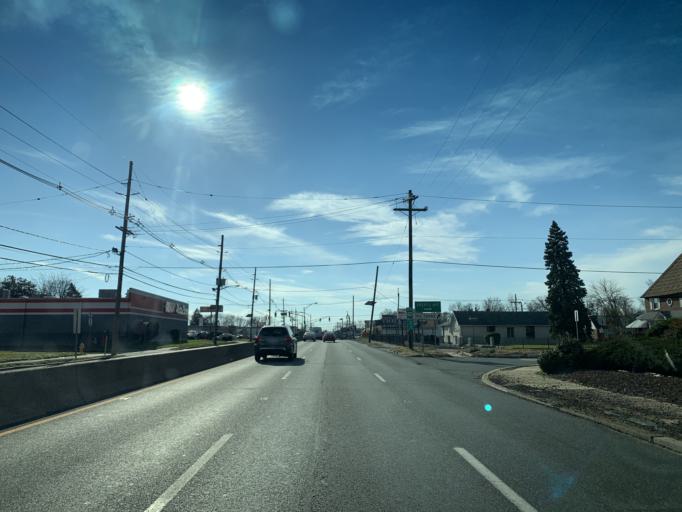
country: US
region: New Jersey
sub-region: Camden County
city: Merchantville
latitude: 39.9425
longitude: -75.0717
